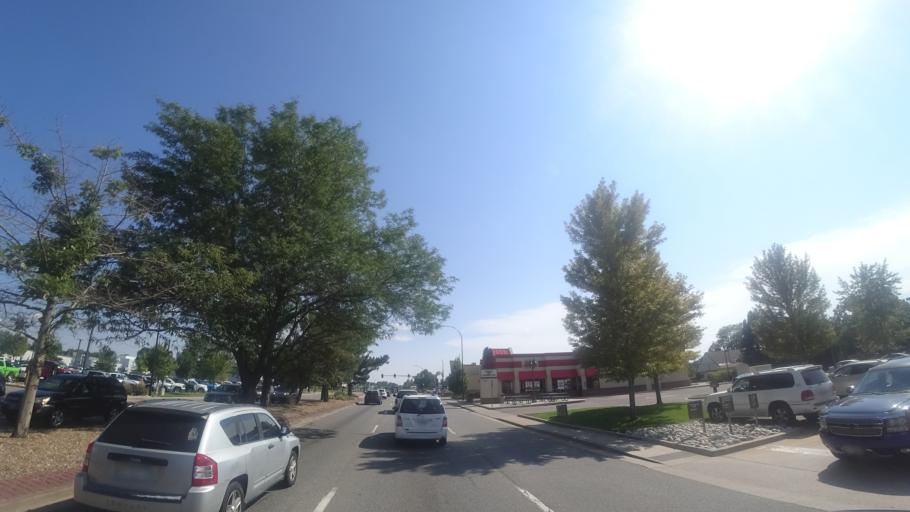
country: US
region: Colorado
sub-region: Arapahoe County
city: Littleton
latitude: 39.6143
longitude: -104.9881
